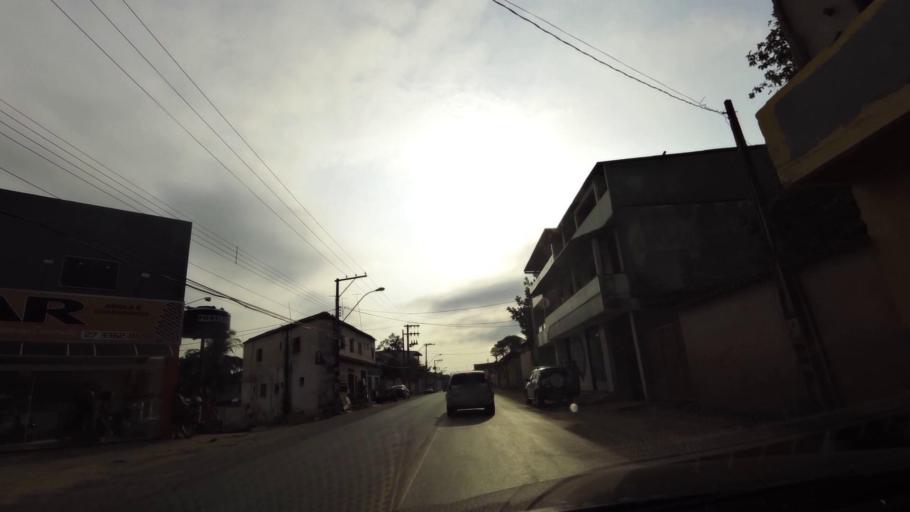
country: BR
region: Espirito Santo
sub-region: Guarapari
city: Guarapari
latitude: -20.6262
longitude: -40.4724
